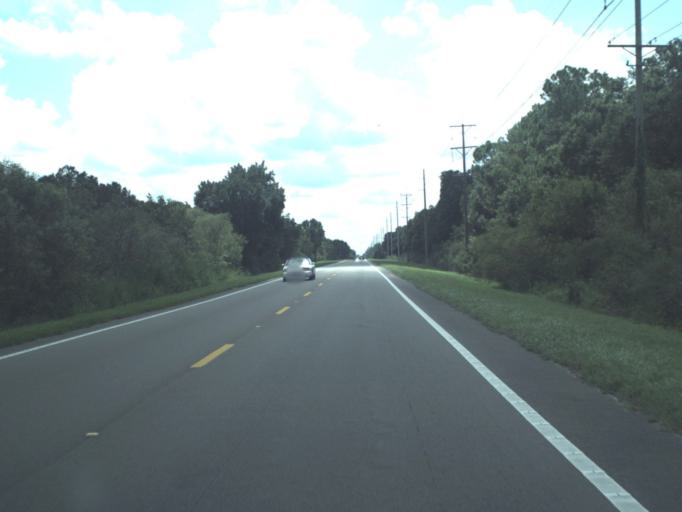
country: US
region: Florida
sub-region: Pasco County
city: Crystal Springs
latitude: 28.1493
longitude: -82.1518
